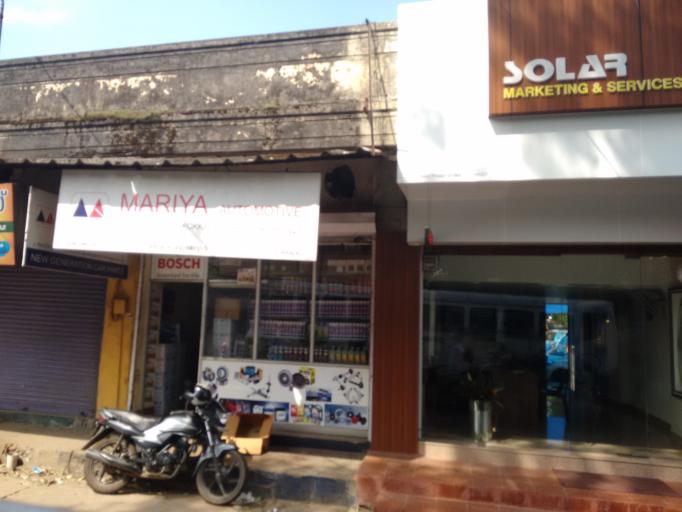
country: IN
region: Kerala
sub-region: Thrissur District
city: Trichur
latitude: 10.5138
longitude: 76.2111
